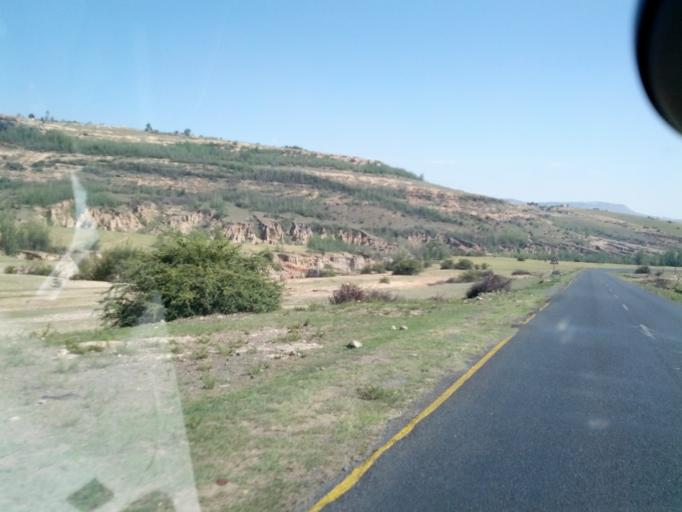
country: LS
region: Berea
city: Teyateyaneng
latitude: -29.1419
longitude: 27.7041
